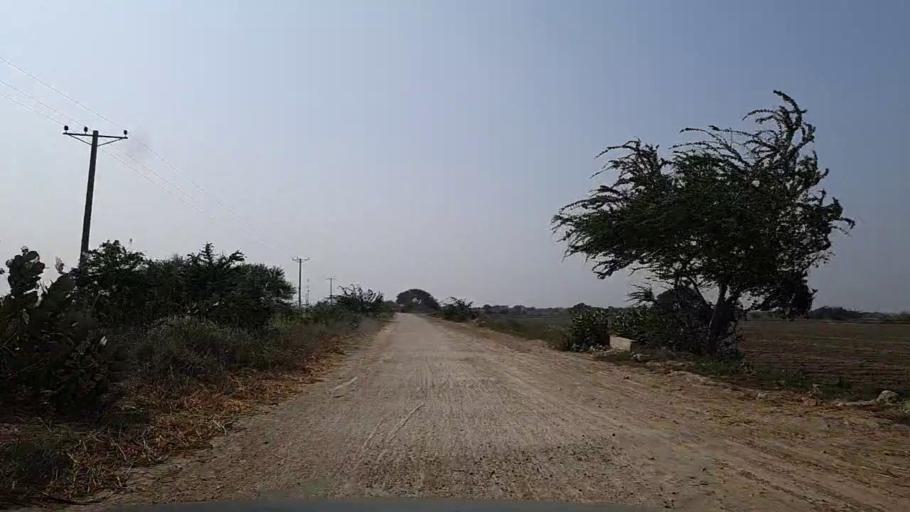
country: PK
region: Sindh
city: Mirpur Sakro
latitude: 24.5280
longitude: 67.5519
